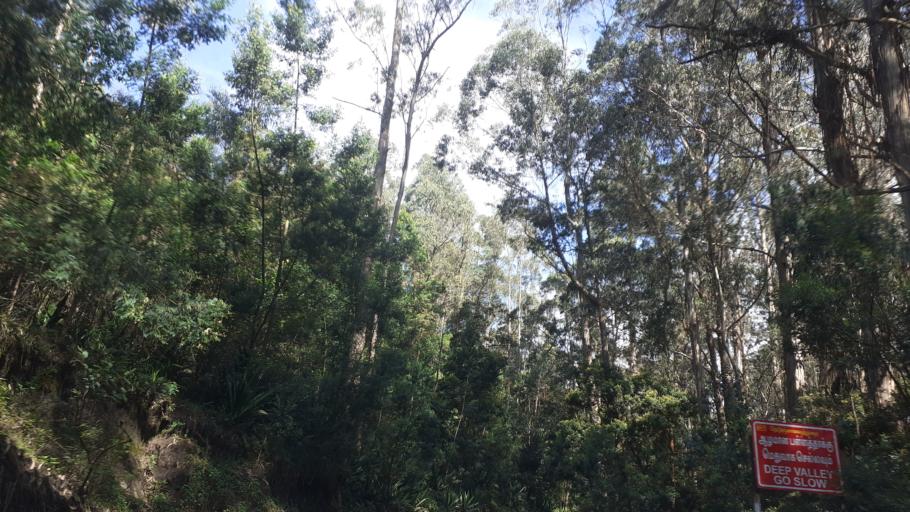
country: IN
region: Tamil Nadu
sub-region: Dindigul
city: Kodaikanal
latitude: 10.2277
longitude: 77.4235
